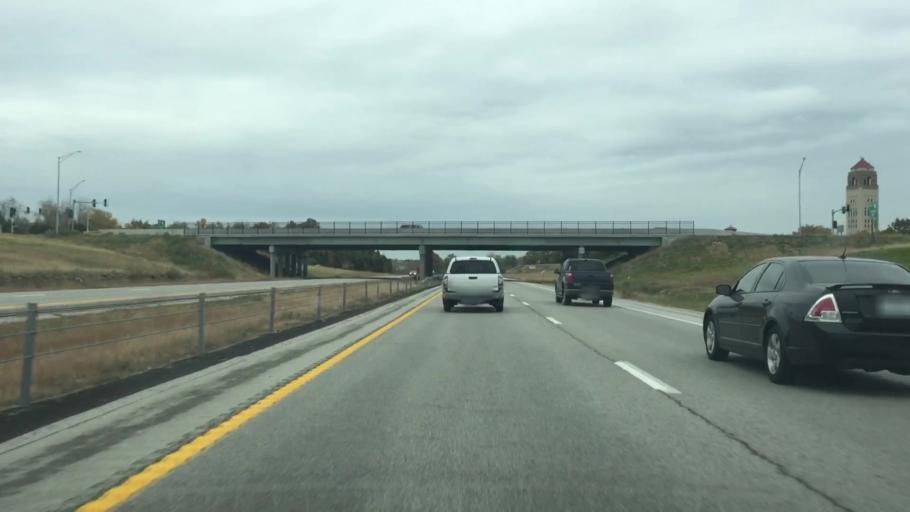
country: US
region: Missouri
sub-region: Jackson County
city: Lees Summit
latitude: 38.9430
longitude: -94.4086
